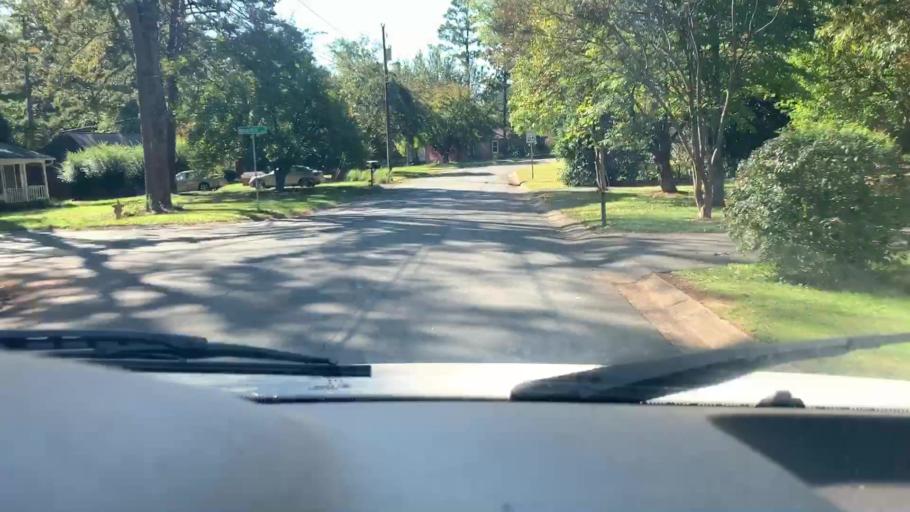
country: US
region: North Carolina
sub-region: Mecklenburg County
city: Charlotte
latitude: 35.2898
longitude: -80.7910
